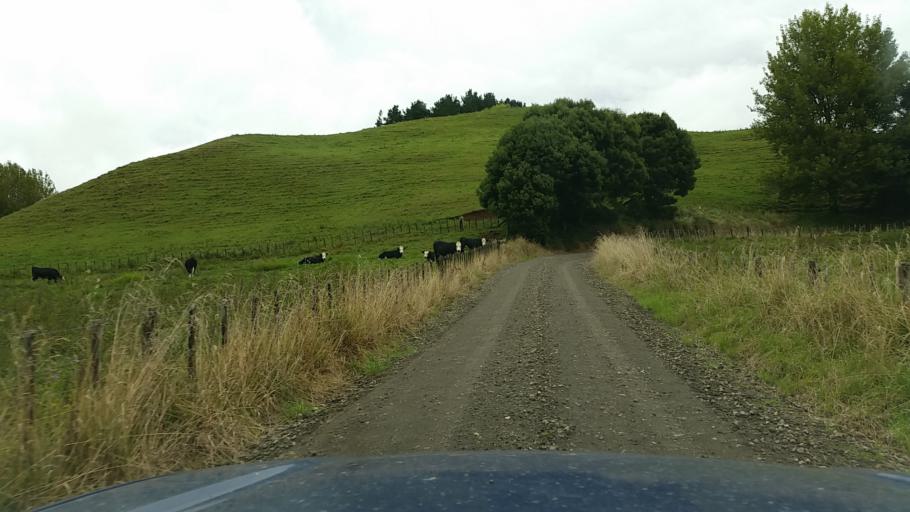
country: NZ
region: Taranaki
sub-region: South Taranaki District
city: Eltham
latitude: -39.2524
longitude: 174.4093
